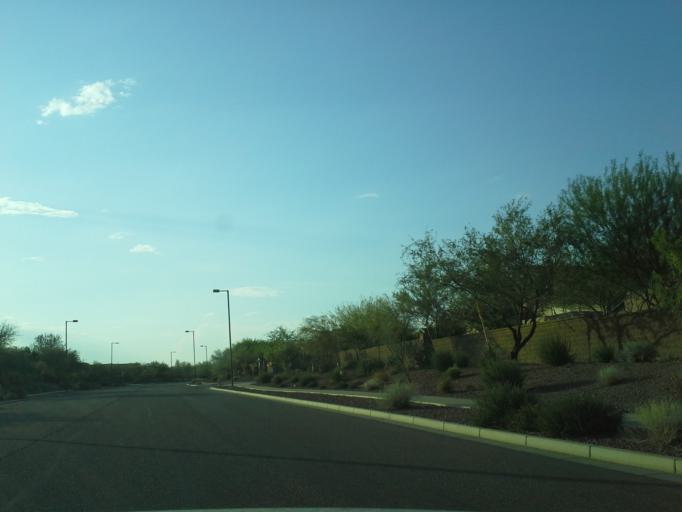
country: US
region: Arizona
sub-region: Maricopa County
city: Anthem
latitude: 33.8662
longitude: -112.1549
